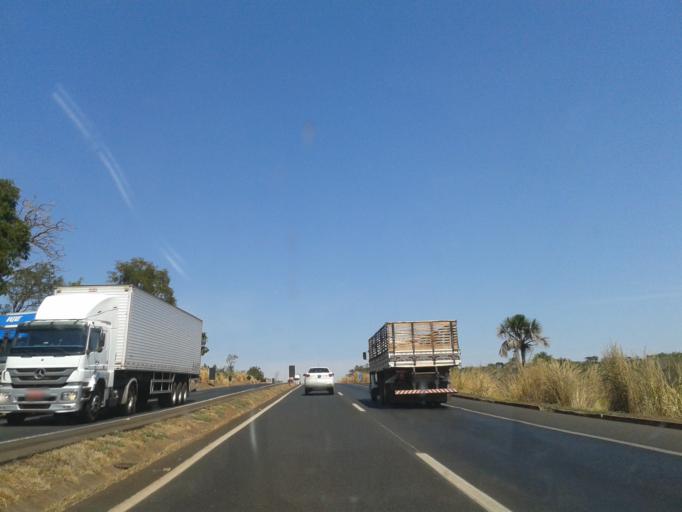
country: BR
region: Minas Gerais
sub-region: Monte Alegre De Minas
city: Monte Alegre de Minas
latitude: -18.8362
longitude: -49.0915
